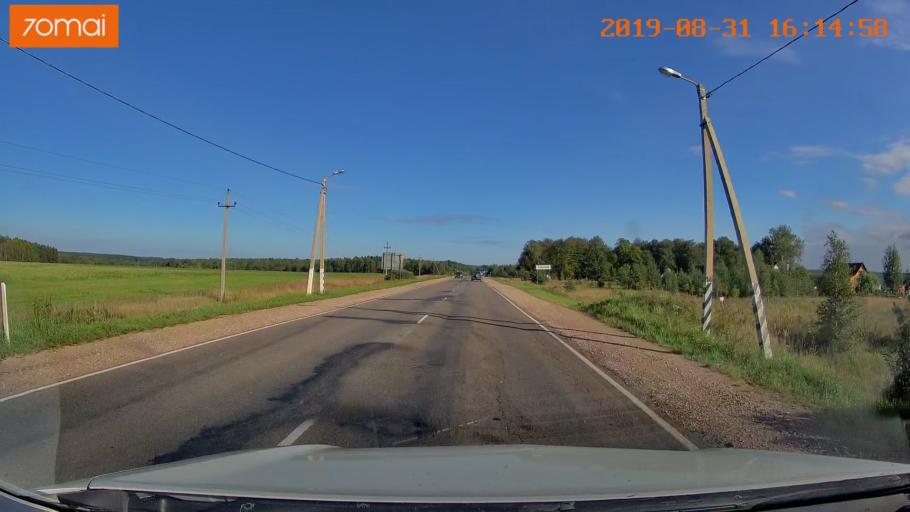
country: RU
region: Kaluga
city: Nikola-Lenivets
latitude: 54.5629
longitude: 35.4790
